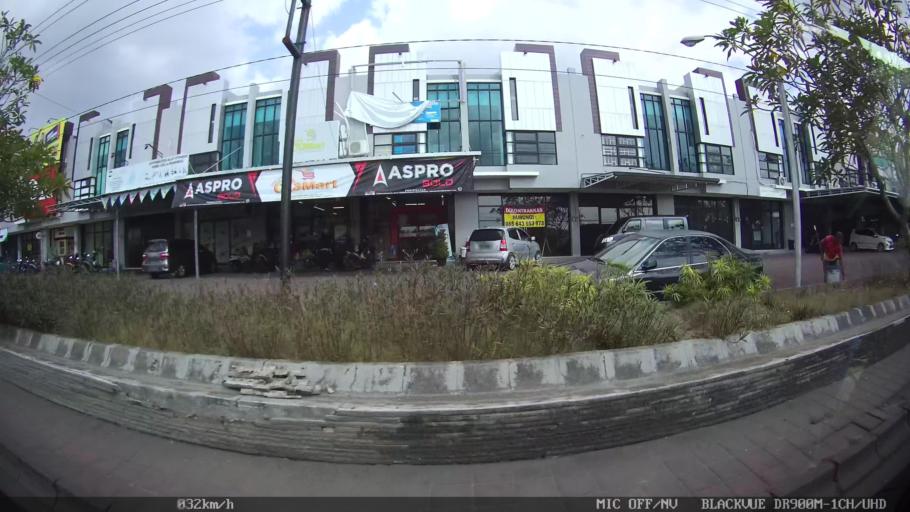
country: ID
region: Daerah Istimewa Yogyakarta
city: Kasihan
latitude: -7.8306
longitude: 110.3171
